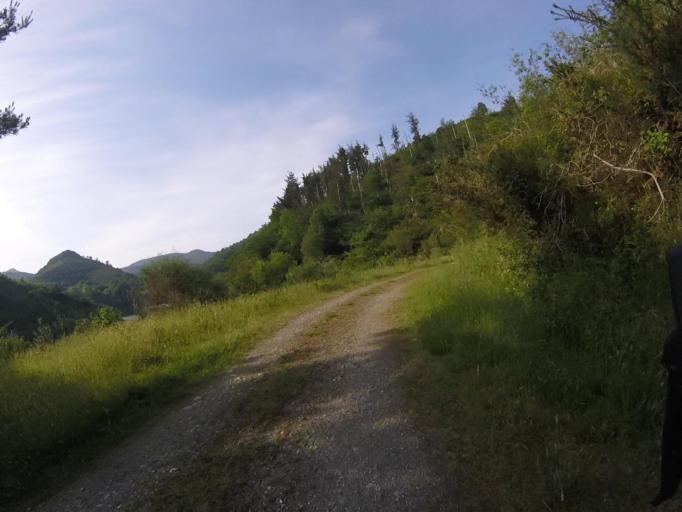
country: ES
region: Navarre
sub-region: Provincia de Navarra
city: Arano
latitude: 43.2261
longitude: -1.8656
